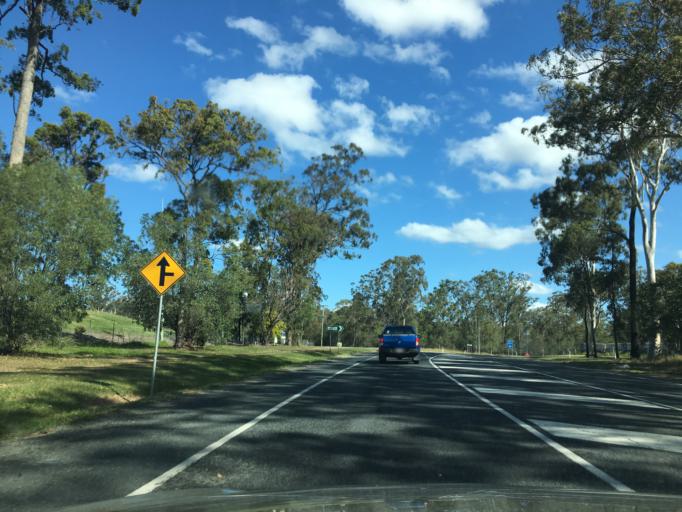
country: AU
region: Queensland
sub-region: Logan
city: Chambers Flat
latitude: -27.7863
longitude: 153.1002
